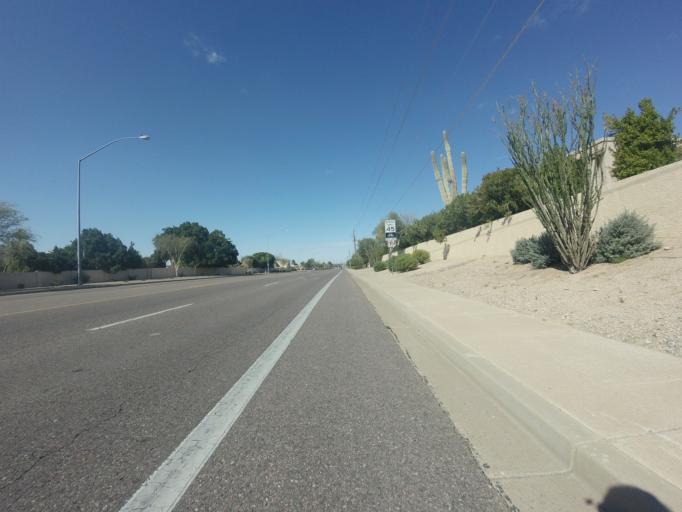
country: US
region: Arizona
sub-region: Maricopa County
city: Mesa
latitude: 33.4664
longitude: -111.6930
